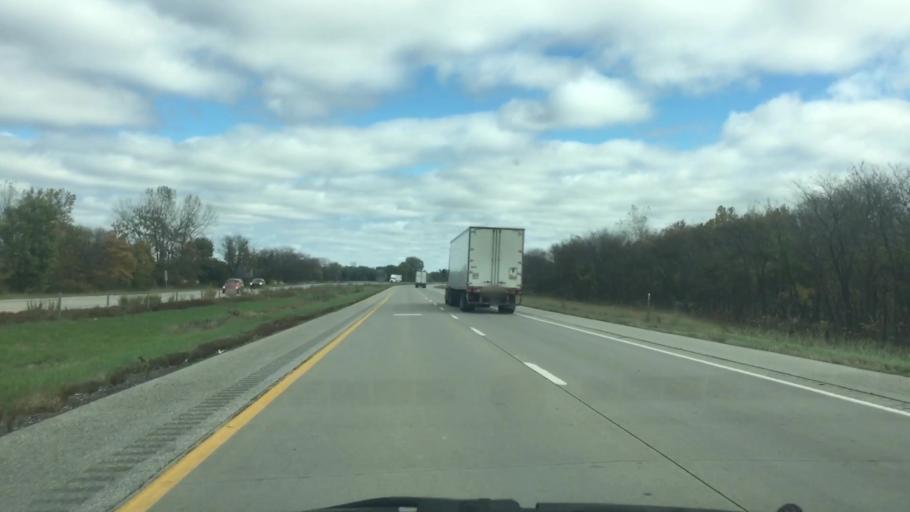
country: US
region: Iowa
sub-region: Jasper County
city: Colfax
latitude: 41.6987
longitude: -93.2151
